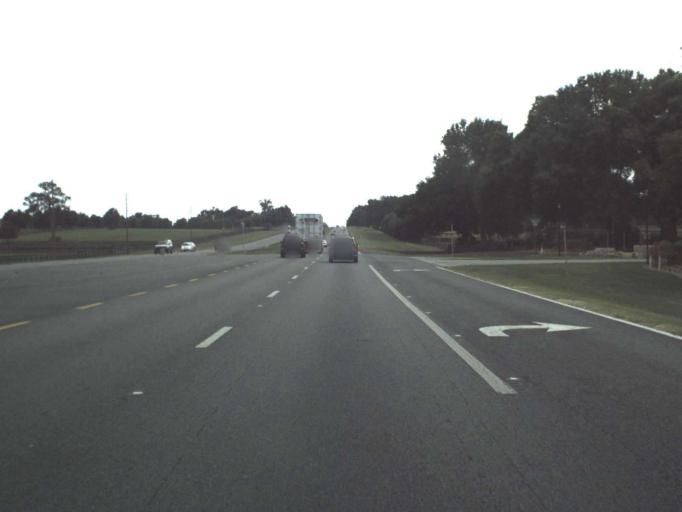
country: US
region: Florida
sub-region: Marion County
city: Citra
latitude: 29.3136
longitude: -82.1519
